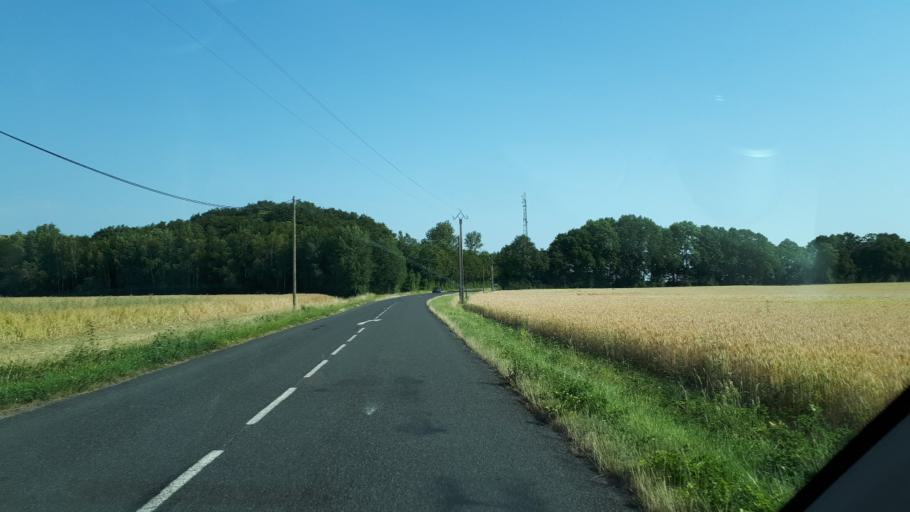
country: FR
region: Centre
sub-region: Departement du Loir-et-Cher
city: Droue
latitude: 47.9766
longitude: 1.0464
